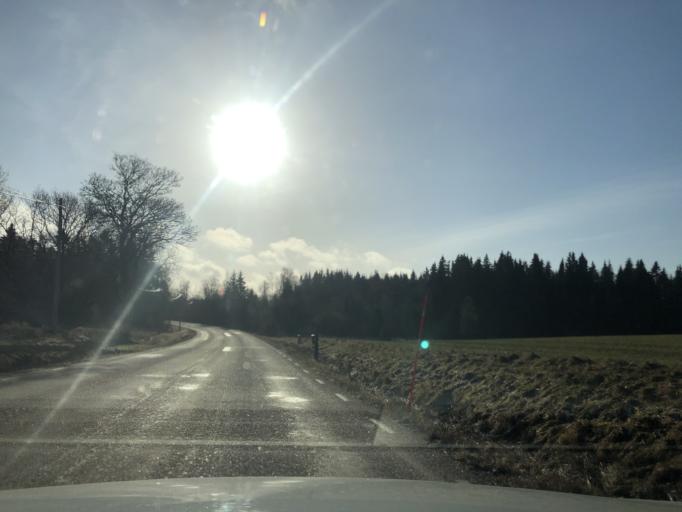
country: SE
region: Vaestra Goetaland
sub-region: Ulricehamns Kommun
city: Ulricehamn
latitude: 57.8129
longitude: 13.5361
